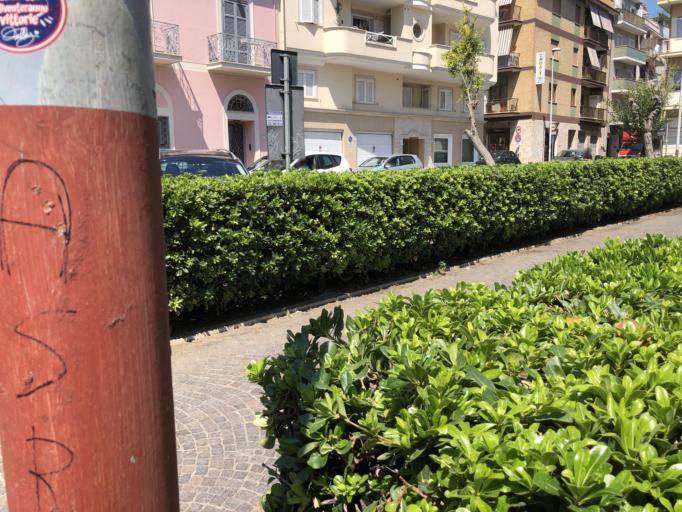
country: IT
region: Latium
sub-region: Citta metropolitana di Roma Capitale
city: Nettuno
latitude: 41.4585
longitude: 12.6558
